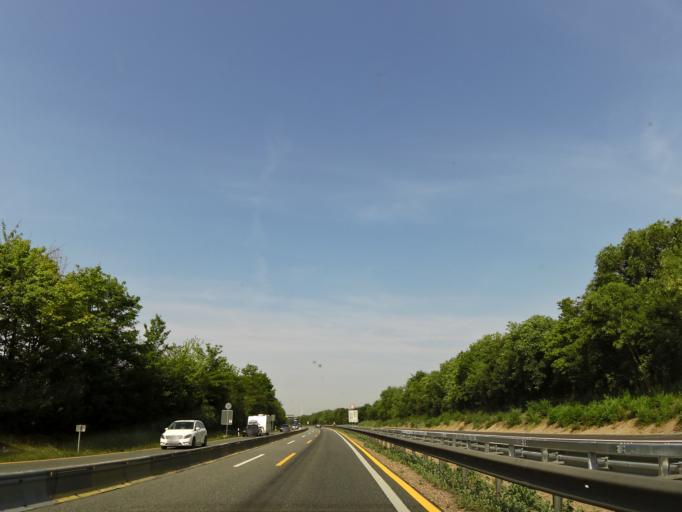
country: DE
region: Rheinland-Pfalz
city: Gundersheim
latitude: 49.7020
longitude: 8.1952
